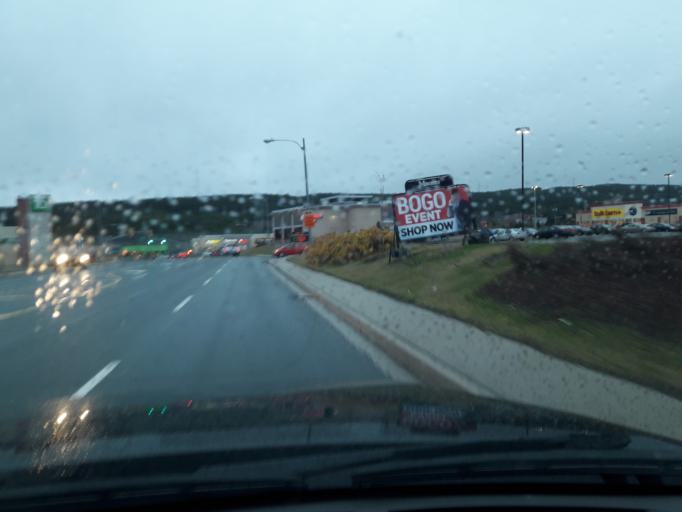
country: CA
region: Newfoundland and Labrador
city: Mount Pearl
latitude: 47.5526
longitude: -52.7808
